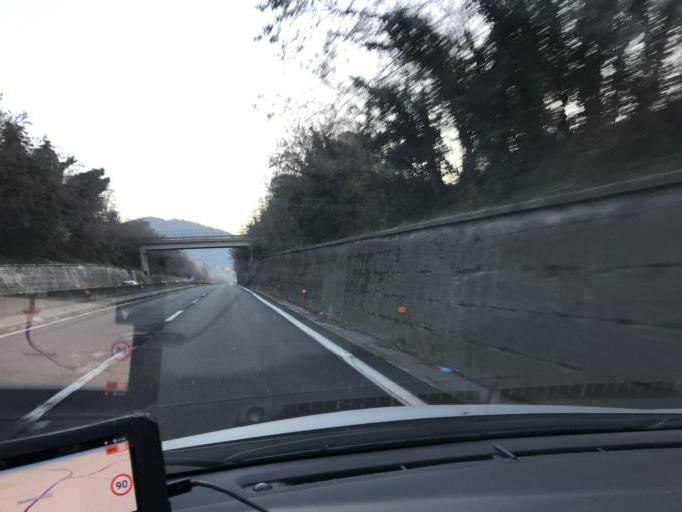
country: IT
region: Umbria
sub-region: Provincia di Terni
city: Terni
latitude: 42.5852
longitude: 12.6592
